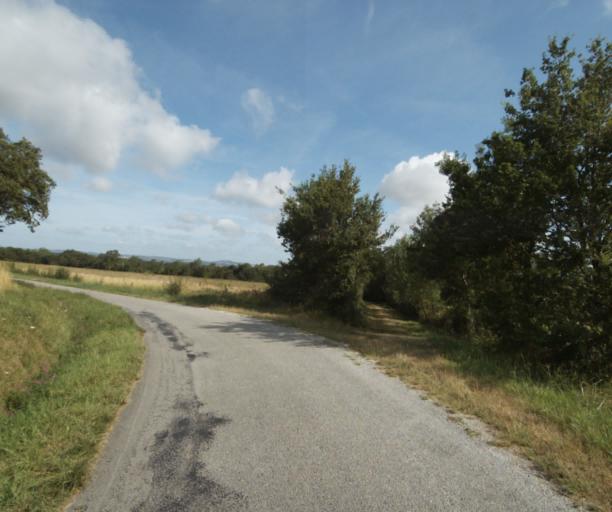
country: FR
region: Midi-Pyrenees
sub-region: Departement du Tarn
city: Soreze
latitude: 43.4670
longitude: 2.0874
